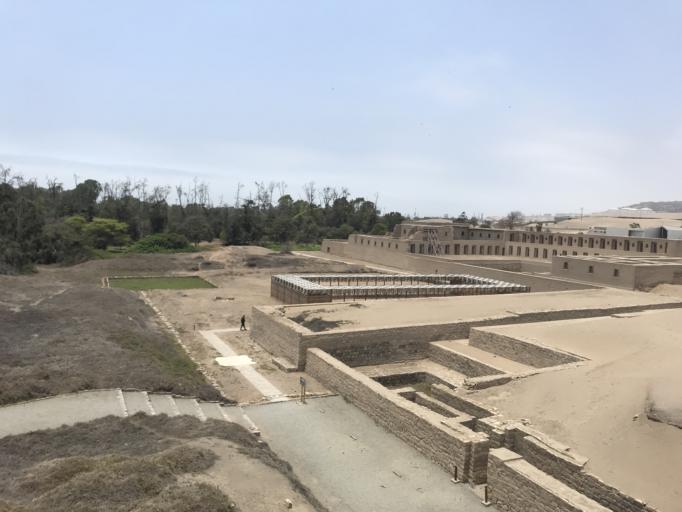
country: PE
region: Lima
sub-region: Lima
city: Punta Hermosa
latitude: -12.2570
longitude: -76.9043
